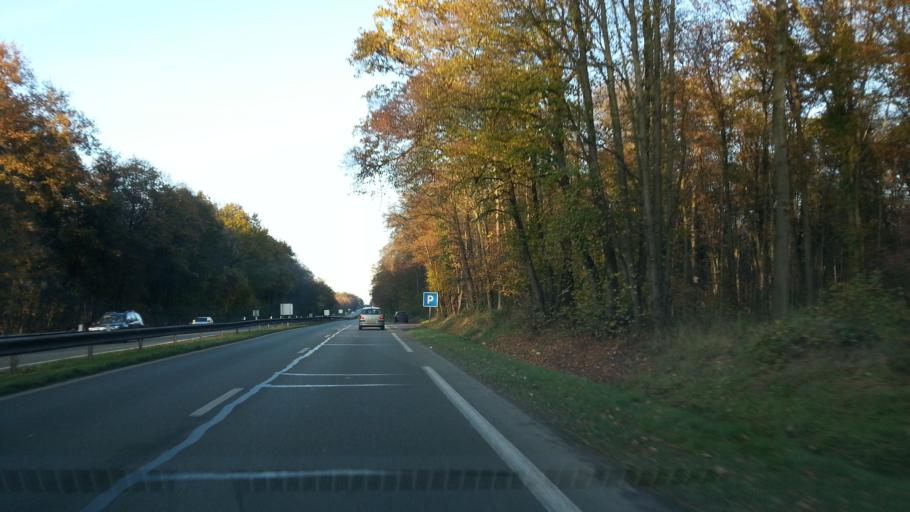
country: FR
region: Picardie
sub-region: Departement de l'Oise
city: Saint-Maximin
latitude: 49.2100
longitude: 2.4636
